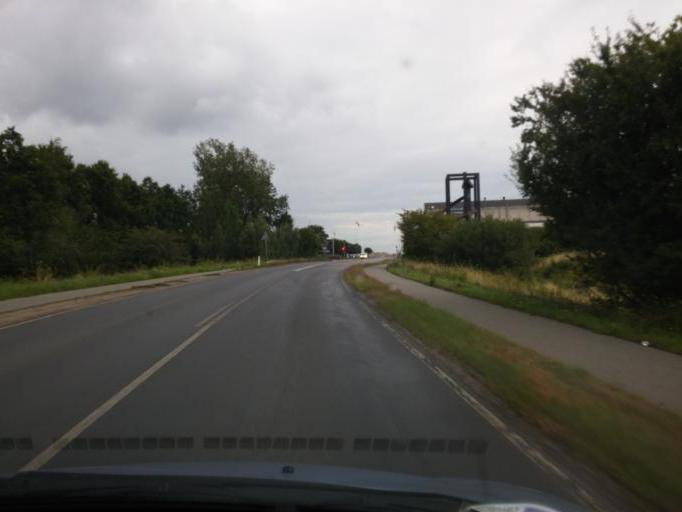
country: DK
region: South Denmark
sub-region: Kerteminde Kommune
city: Munkebo
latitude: 55.4658
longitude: 10.5375
